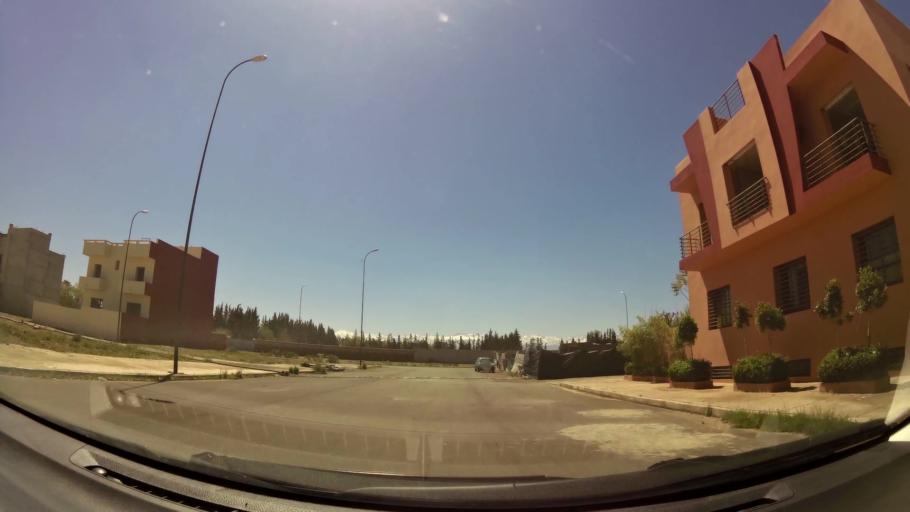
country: MA
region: Marrakech-Tensift-Al Haouz
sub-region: Marrakech
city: Marrakesh
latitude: 31.5504
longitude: -7.9775
